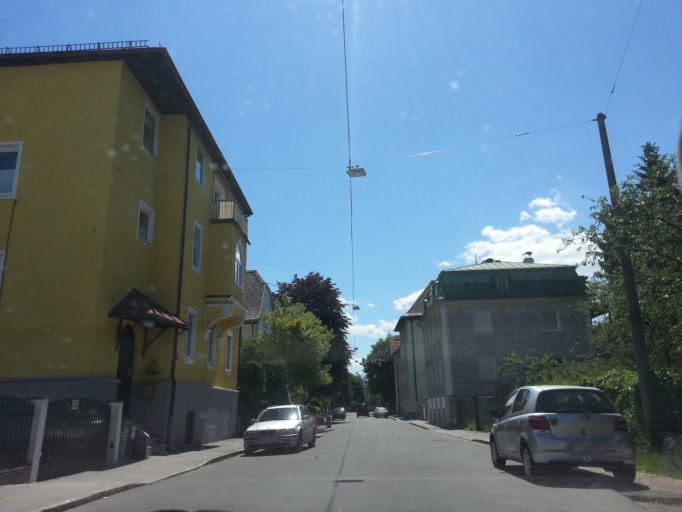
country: AT
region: Salzburg
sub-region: Salzburg Stadt
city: Salzburg
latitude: 47.8026
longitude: 13.0309
